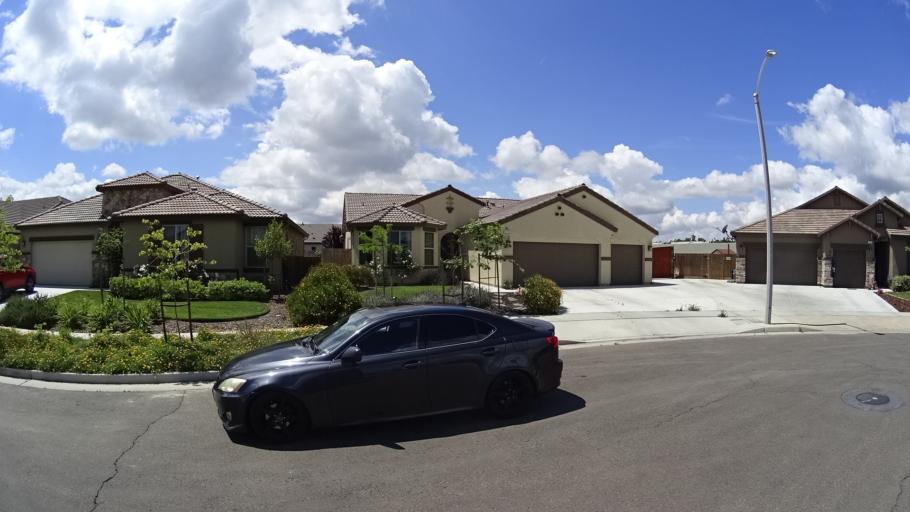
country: US
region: California
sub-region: Kings County
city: Lucerne
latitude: 36.3698
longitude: -119.6631
